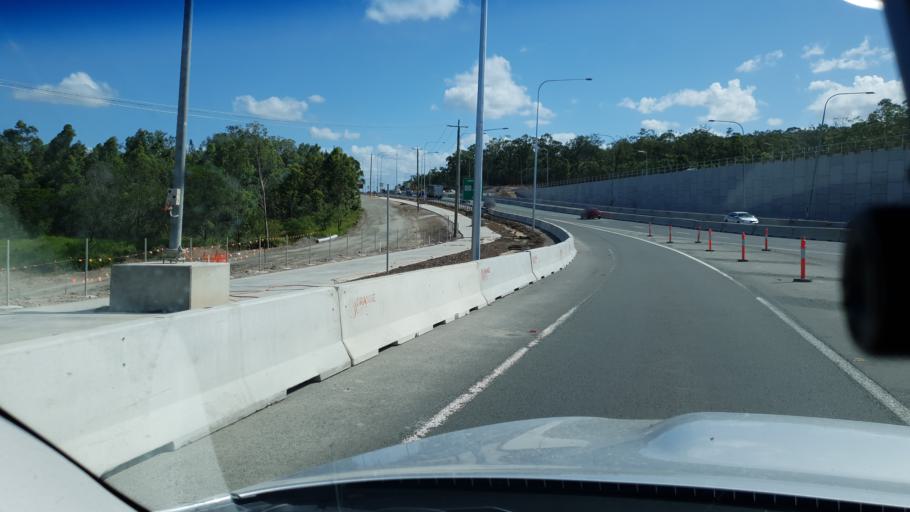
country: AU
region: Queensland
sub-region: Brisbane
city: Sunnybank Hills
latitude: -27.6483
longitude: 153.0417
